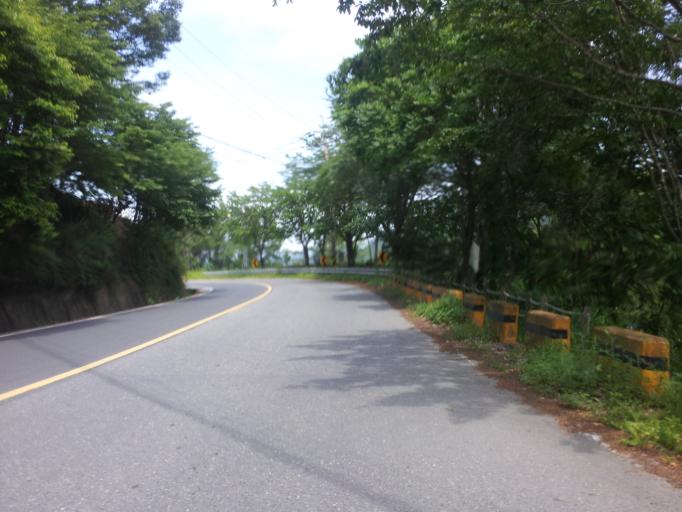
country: KR
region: Daejeon
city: Sintansin
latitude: 36.4297
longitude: 127.4675
